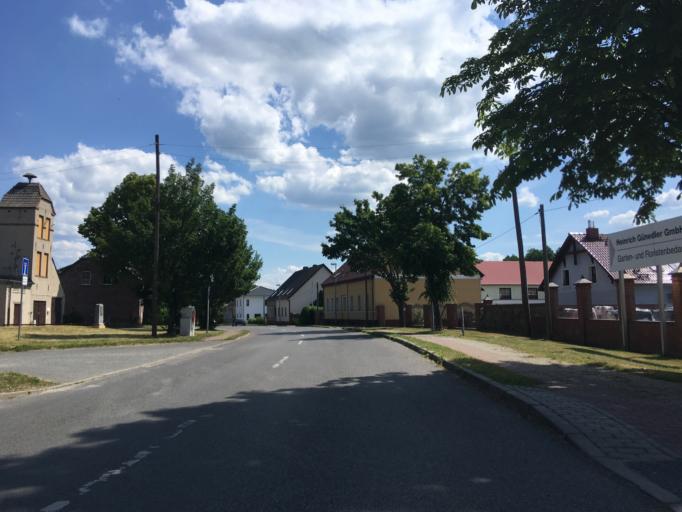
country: DE
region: Brandenburg
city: Neuenhagen
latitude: 52.5496
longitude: 13.6864
